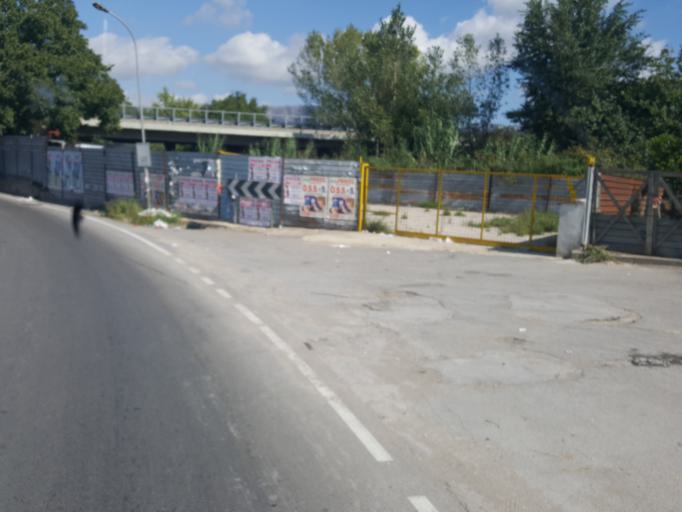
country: IT
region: Campania
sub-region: Provincia di Napoli
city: Nola
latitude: 40.9301
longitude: 14.5110
